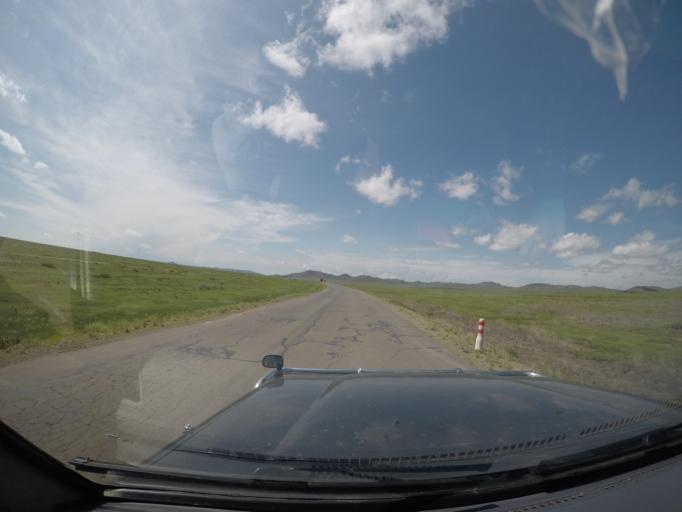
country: MN
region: Hentiy
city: Herlen
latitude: 47.3810
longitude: 110.4627
